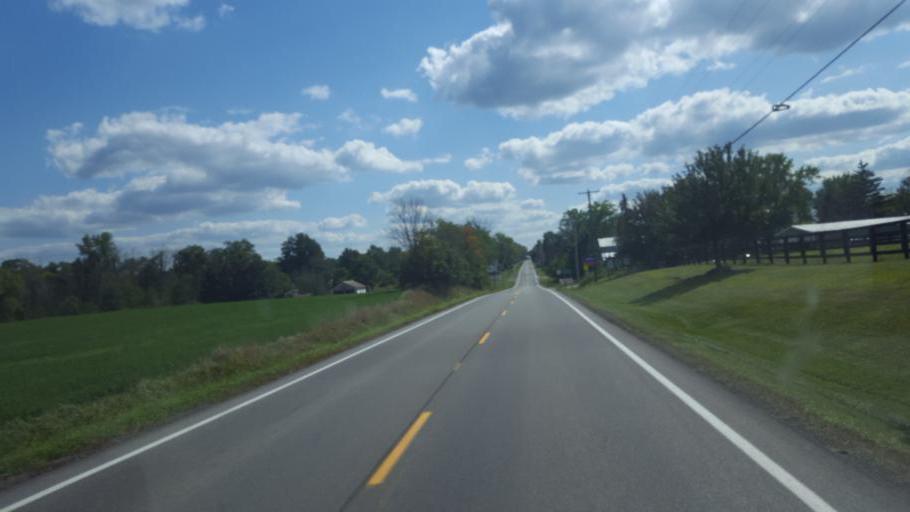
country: US
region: Ohio
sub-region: Wayne County
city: West Salem
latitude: 40.9531
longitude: -82.2148
